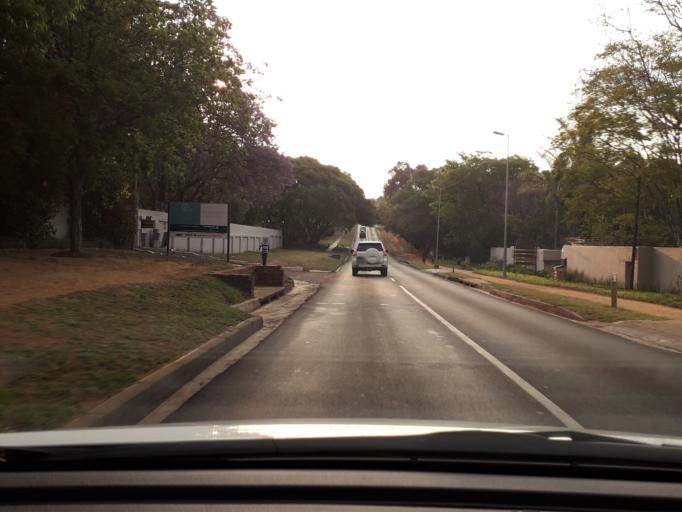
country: ZA
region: Gauteng
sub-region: City of Johannesburg Metropolitan Municipality
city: Midrand
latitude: -26.0475
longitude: 28.0291
